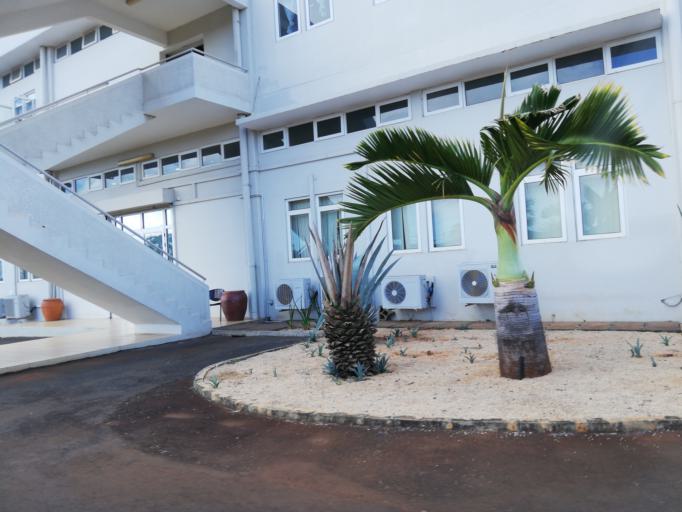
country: MU
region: Black River
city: Petite Riviere
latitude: -20.1893
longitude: 57.4643
